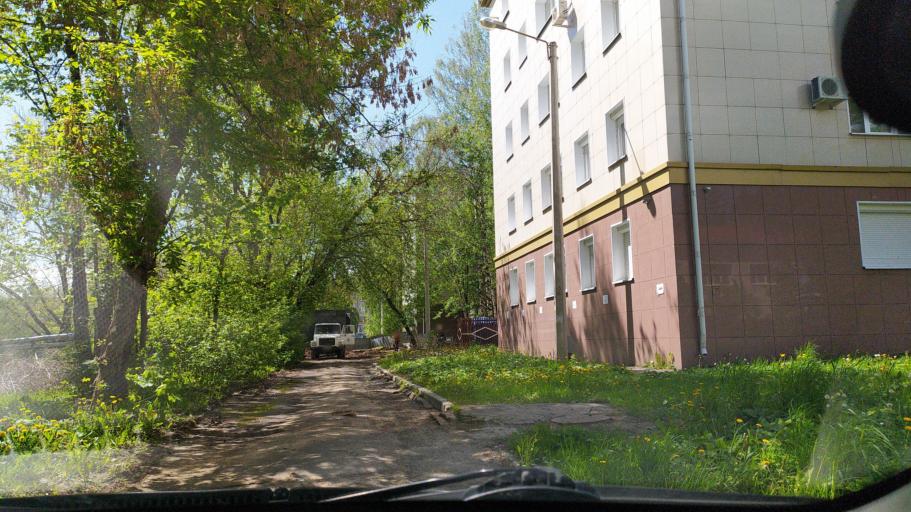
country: RU
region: Chuvashia
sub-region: Cheboksarskiy Rayon
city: Cheboksary
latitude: 56.1411
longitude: 47.2024
